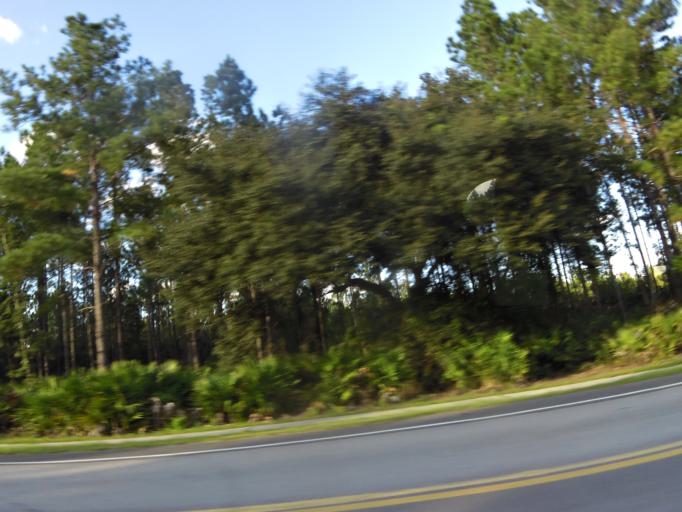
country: US
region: Florida
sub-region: Saint Johns County
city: Fruit Cove
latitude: 30.0585
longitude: -81.6308
